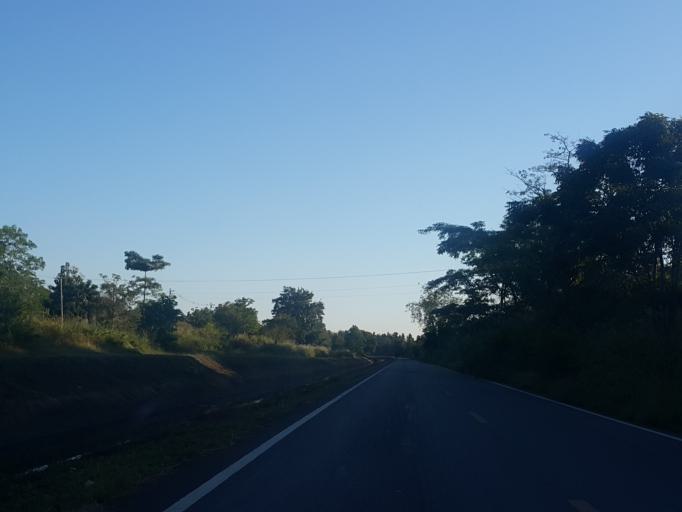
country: TH
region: Chiang Mai
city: San Sai
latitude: 18.9061
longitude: 99.1488
